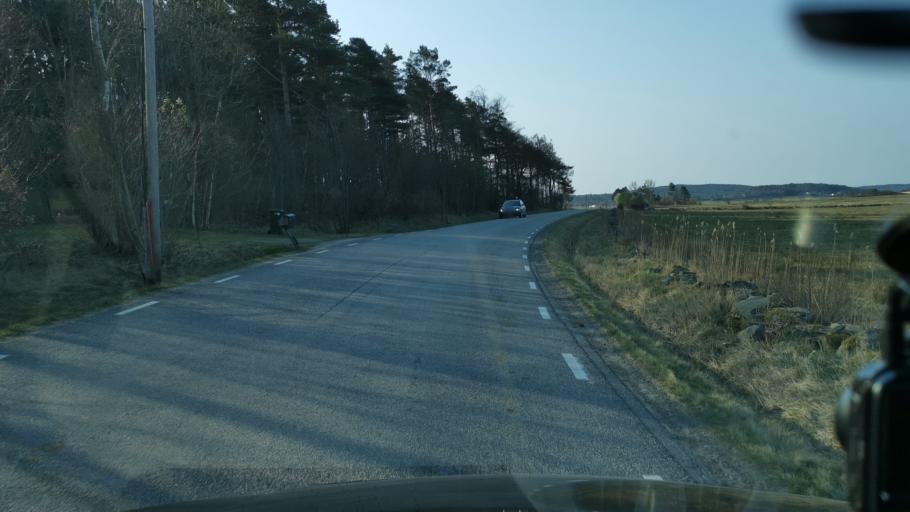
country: SE
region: Vaestra Goetaland
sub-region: Kungalvs Kommun
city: Kode
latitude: 57.9605
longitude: 11.8224
